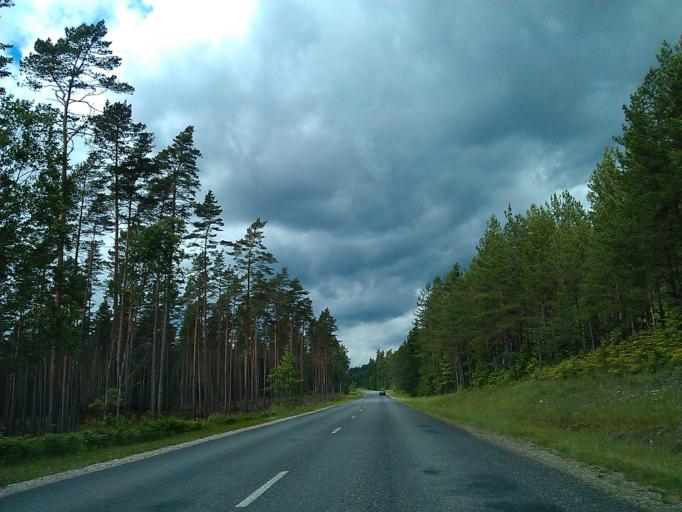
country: LV
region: Talsu Rajons
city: Stende
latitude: 57.0849
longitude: 22.4234
